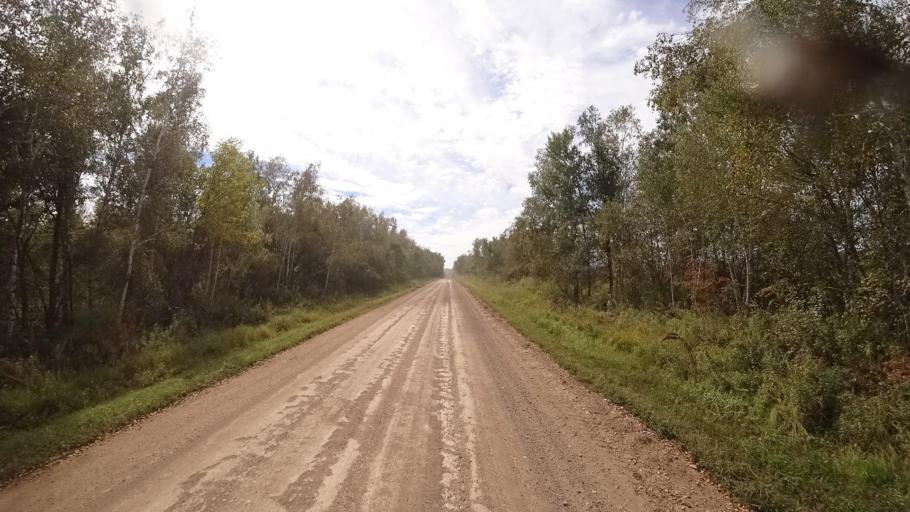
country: RU
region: Primorskiy
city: Yakovlevka
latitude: 44.5591
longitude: 133.5913
